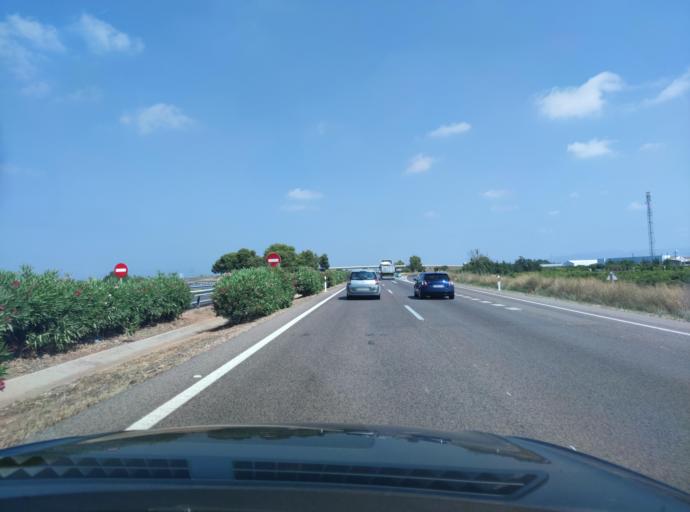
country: ES
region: Valencia
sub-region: Provincia de Castello
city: Alquerias del Nino Perdido
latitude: 39.8937
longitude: -0.1297
